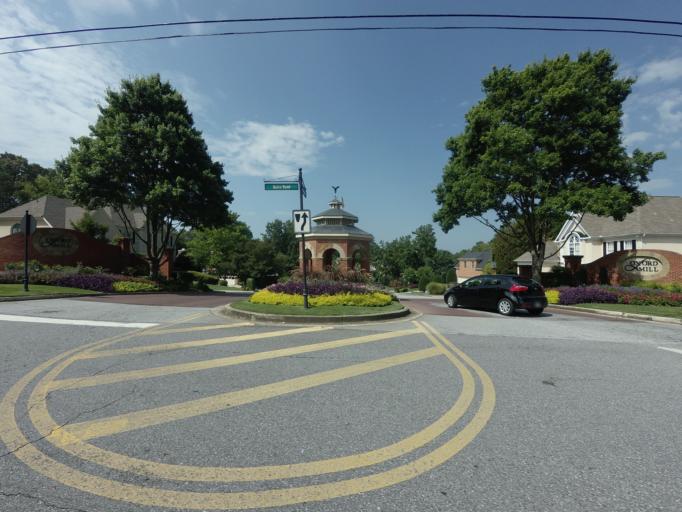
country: US
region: Georgia
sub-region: Fulton County
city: Johns Creek
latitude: 34.0324
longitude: -84.2339
